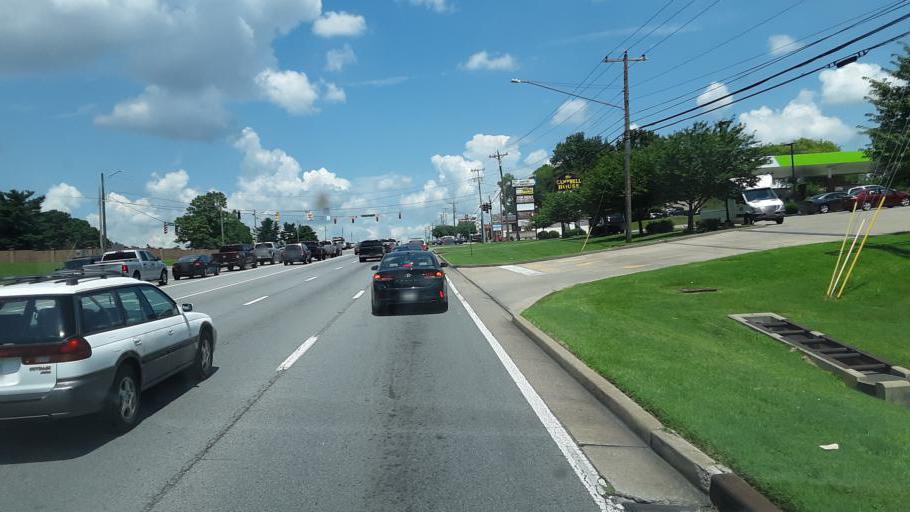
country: US
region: Kentucky
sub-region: Christian County
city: Fort Campbell North
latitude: 36.6141
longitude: -87.4304
